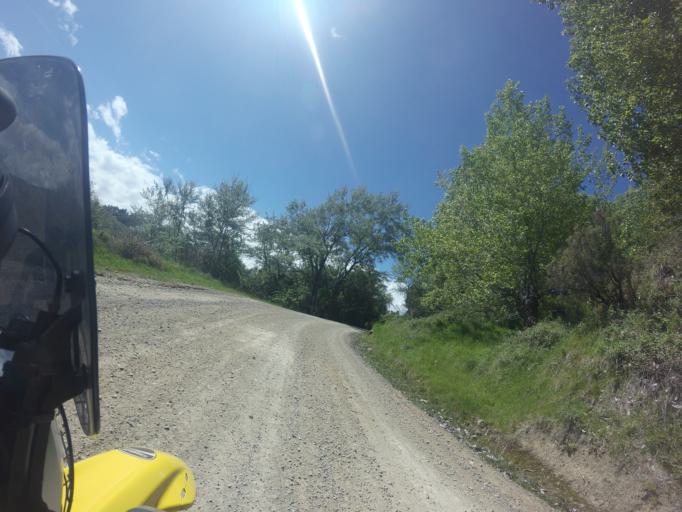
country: NZ
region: Hawke's Bay
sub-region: Wairoa District
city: Wairoa
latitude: -38.9912
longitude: 177.7180
